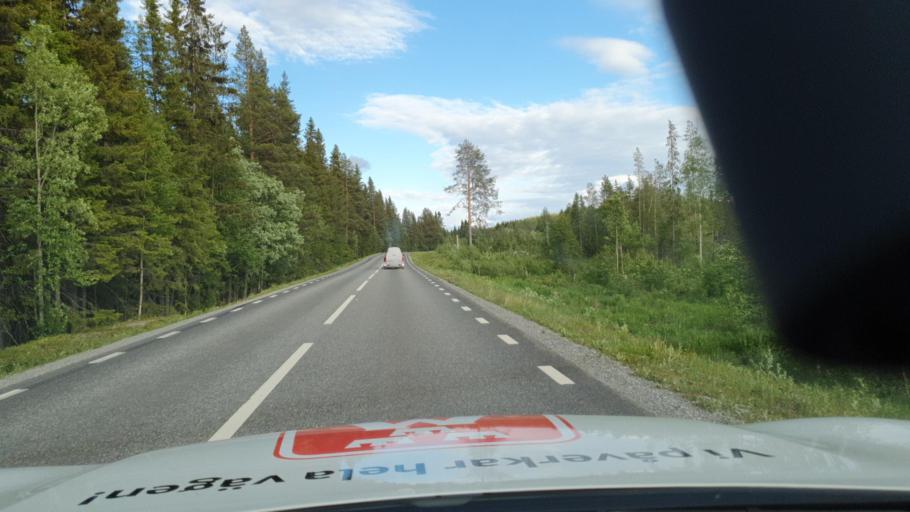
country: SE
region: Vaesterbotten
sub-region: Storumans Kommun
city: Storuman
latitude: 64.9872
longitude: 17.1025
